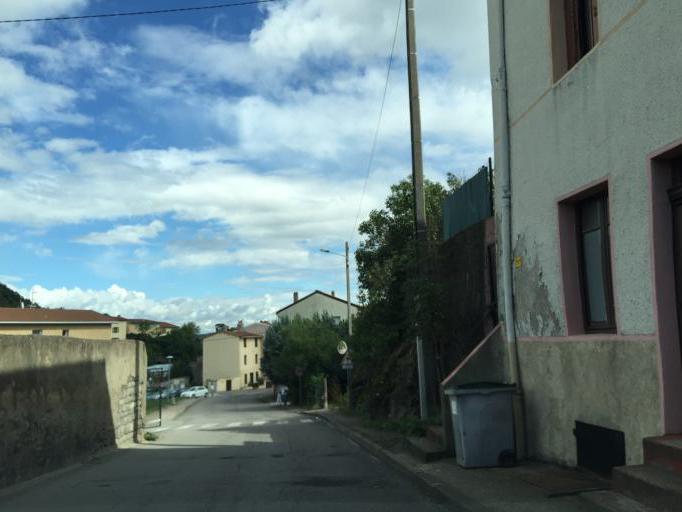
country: FR
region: Rhone-Alpes
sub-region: Departement de la Loire
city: Lorette
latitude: 45.5211
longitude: 4.5905
